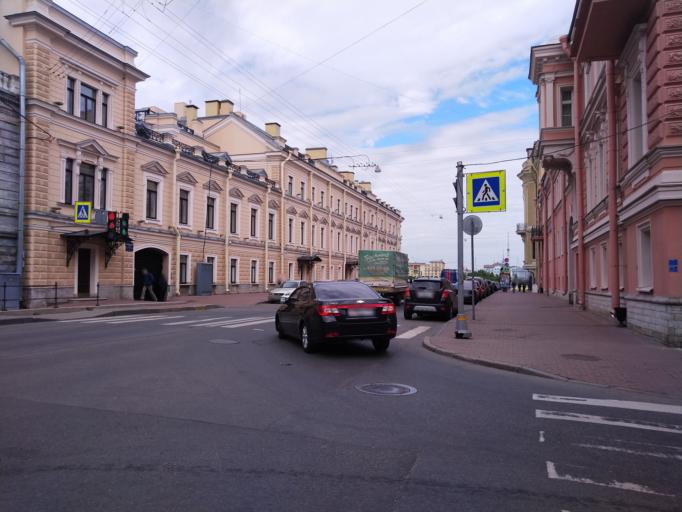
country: RU
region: St.-Petersburg
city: Centralniy
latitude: 59.9480
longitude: 30.3419
